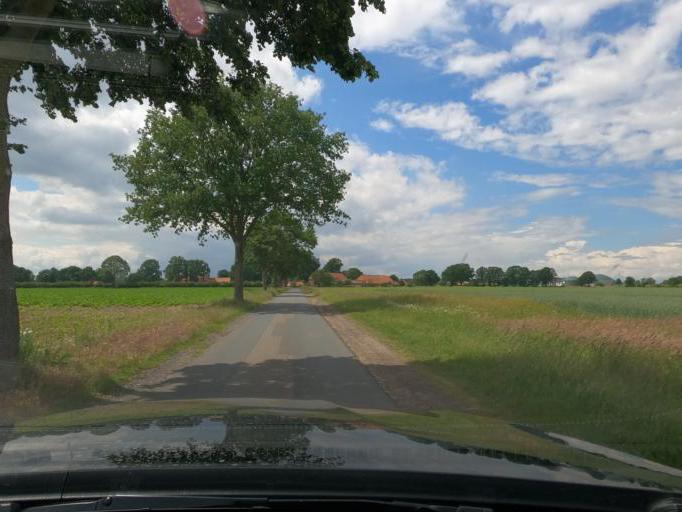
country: DE
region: Lower Saxony
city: Steimbke
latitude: 52.6309
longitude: 9.3984
